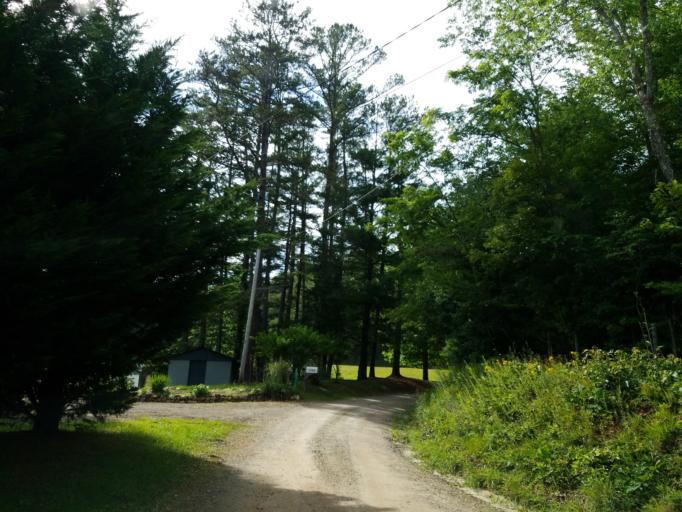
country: US
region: Georgia
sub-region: Union County
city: Blairsville
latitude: 34.7372
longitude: -84.0608
